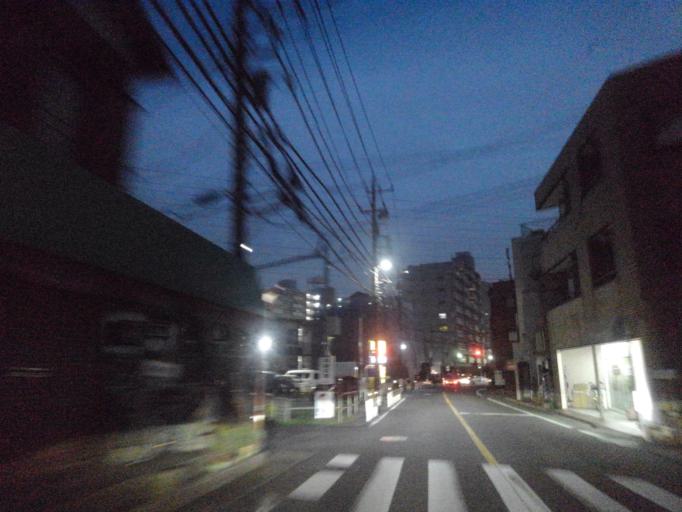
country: JP
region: Saitama
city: Tokorozawa
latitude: 35.8100
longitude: 139.4504
